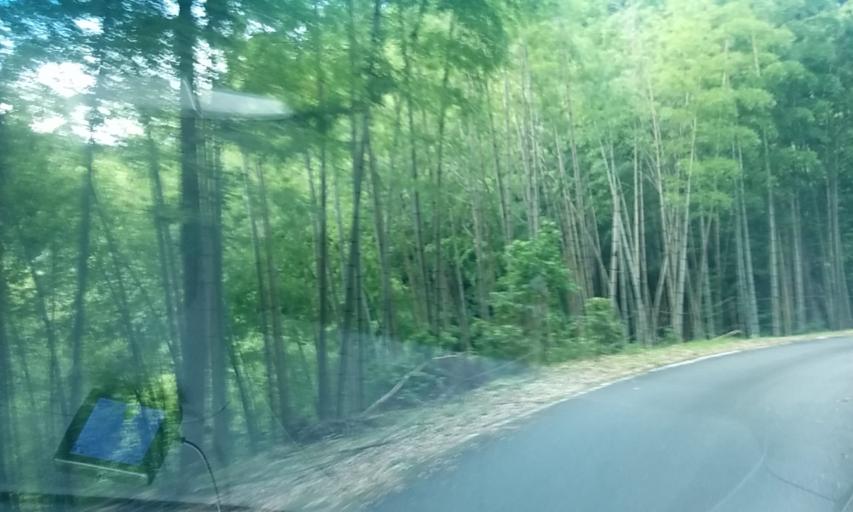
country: JP
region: Hyogo
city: Sasayama
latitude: 35.1736
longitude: 135.2056
